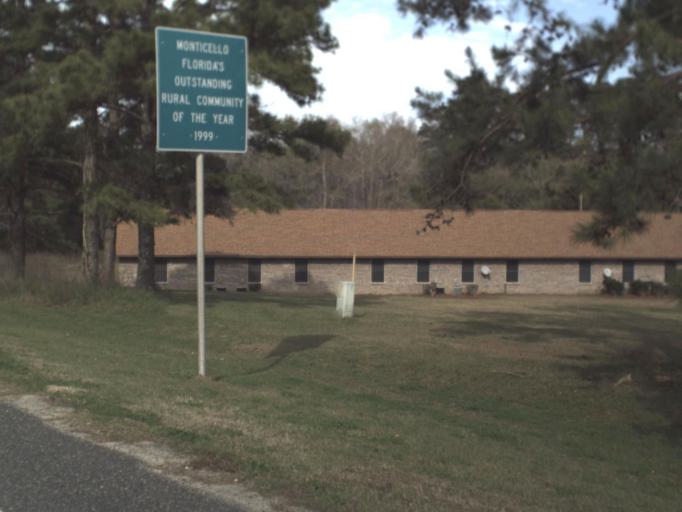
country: US
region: Florida
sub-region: Jefferson County
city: Monticello
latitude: 30.5243
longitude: -83.8726
